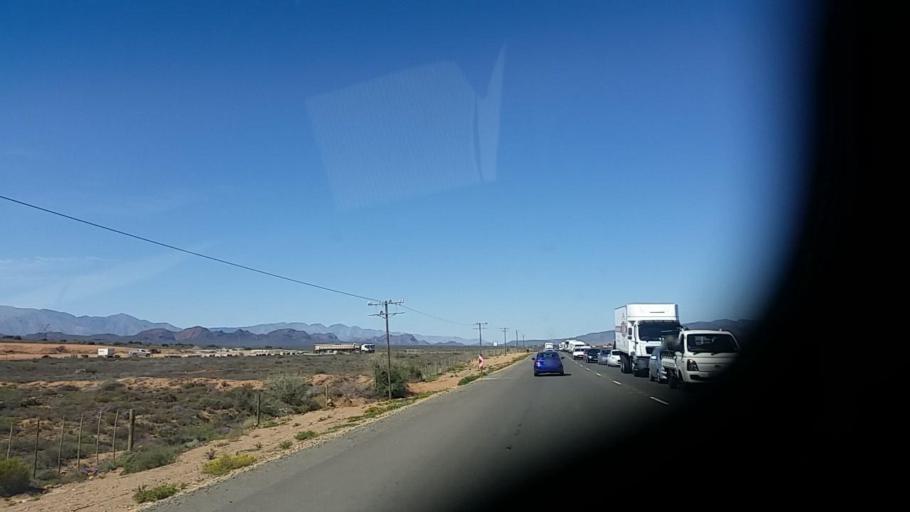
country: ZA
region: Western Cape
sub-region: Eden District Municipality
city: Oudtshoorn
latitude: -33.5861
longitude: 22.2771
